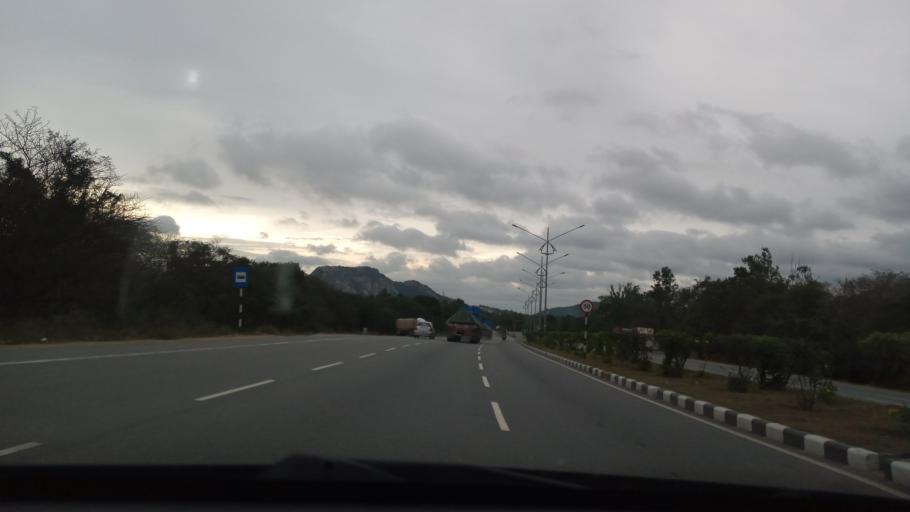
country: IN
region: Tamil Nadu
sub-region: Vellore
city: Jolarpettai
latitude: 12.5396
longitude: 78.4126
